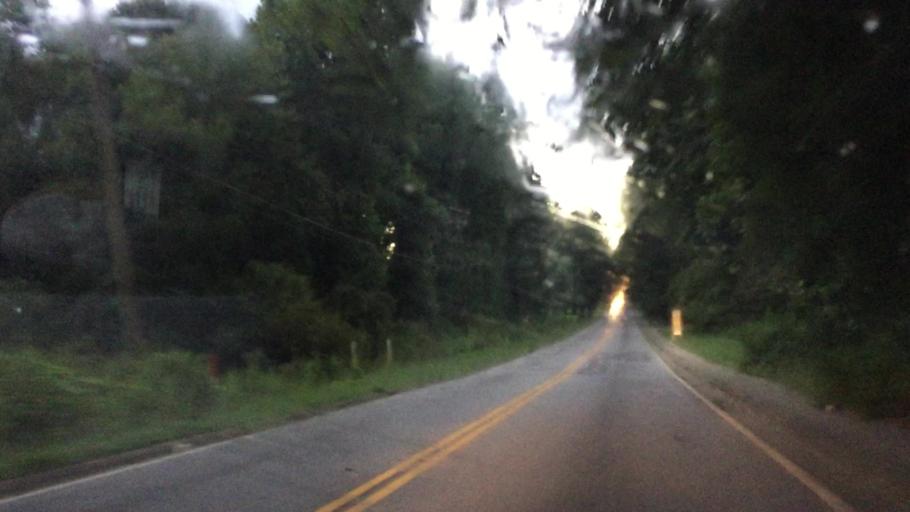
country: US
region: Georgia
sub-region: Clayton County
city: Riverdale
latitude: 33.5615
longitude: -84.4042
